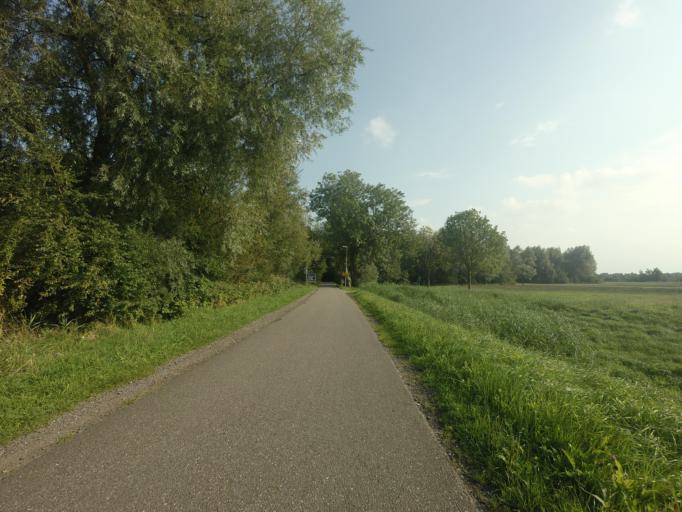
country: NL
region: Groningen
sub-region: Gemeente Groningen
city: Groningen
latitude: 53.1849
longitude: 6.5661
